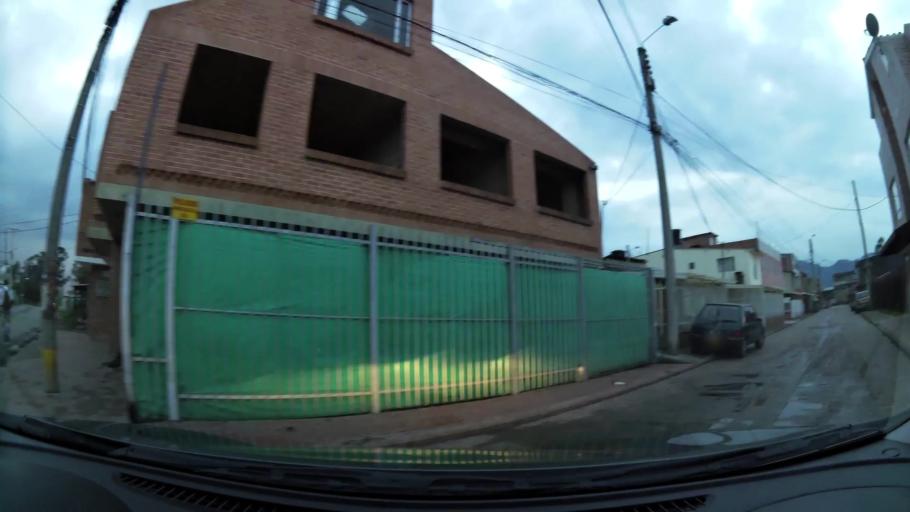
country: CO
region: Cundinamarca
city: Chia
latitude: 4.8405
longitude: -74.0598
